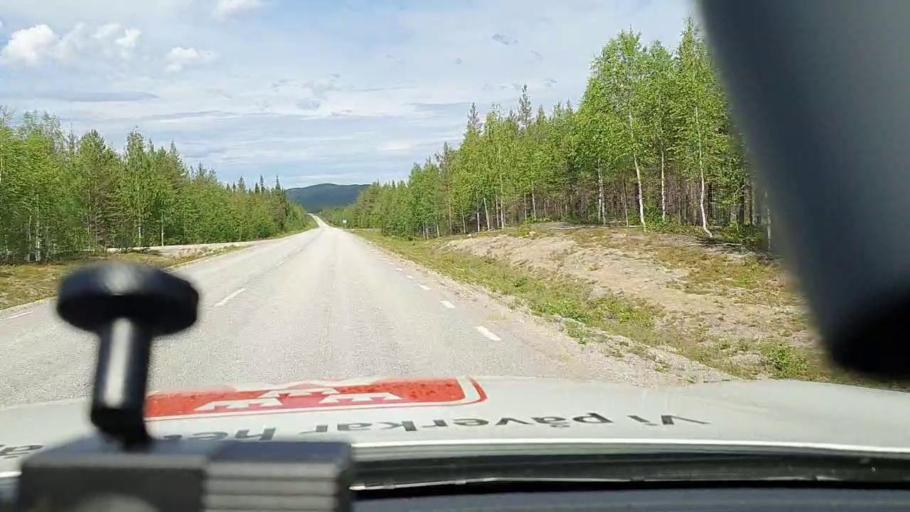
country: SE
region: Norrbotten
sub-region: Jokkmokks Kommun
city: Jokkmokk
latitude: 66.5442
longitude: 20.1378
